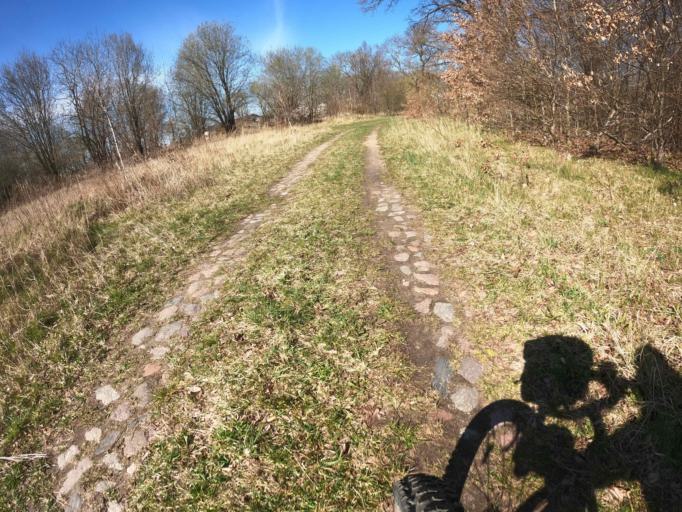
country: PL
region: West Pomeranian Voivodeship
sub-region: Powiat gryficki
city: Brojce
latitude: 54.0005
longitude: 15.3816
